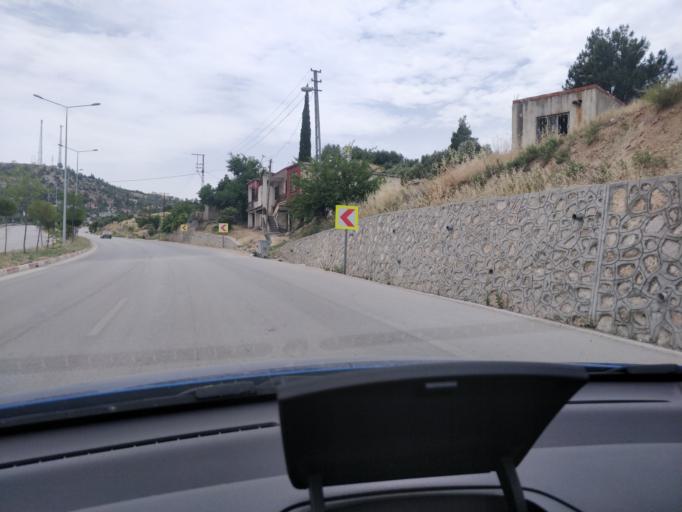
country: TR
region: Mersin
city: Mut
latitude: 36.6567
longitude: 33.4225
